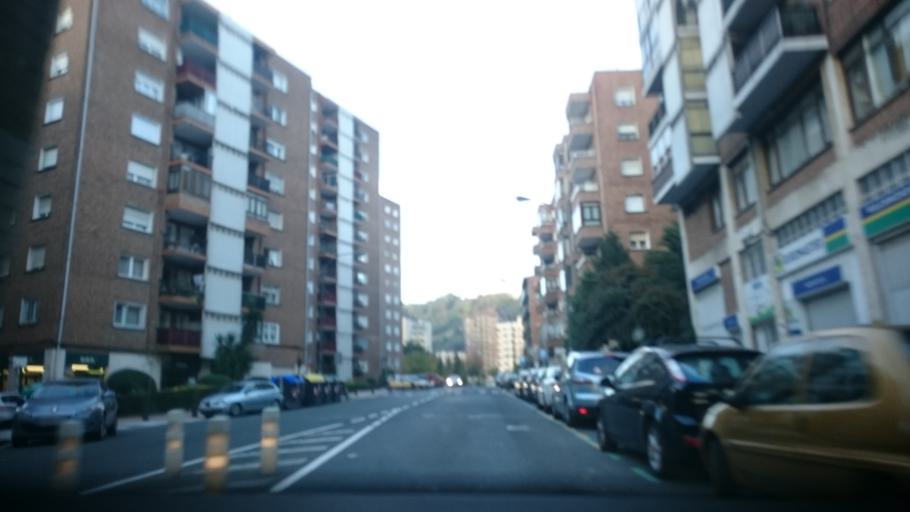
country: ES
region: Basque Country
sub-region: Bizkaia
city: Santutxu
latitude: 43.2596
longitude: -2.9173
